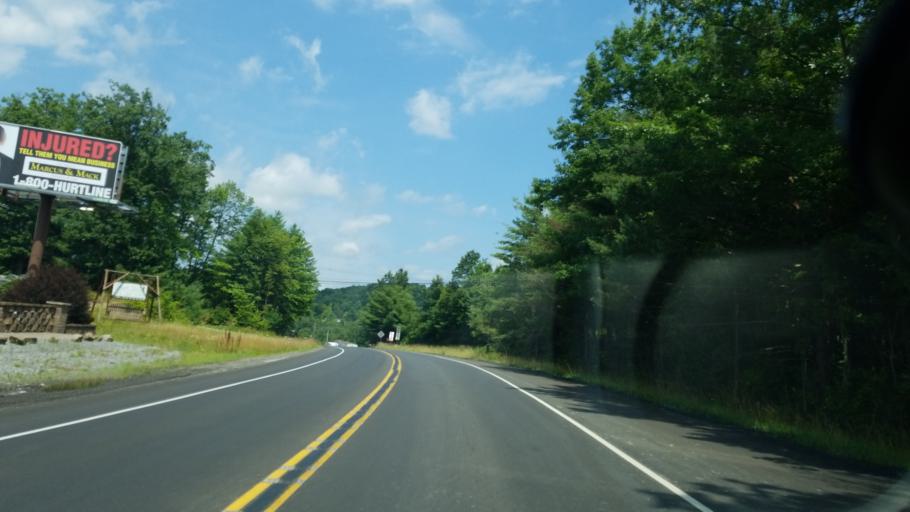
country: US
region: Pennsylvania
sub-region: Jefferson County
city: Brookville
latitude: 41.1792
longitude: -79.0986
